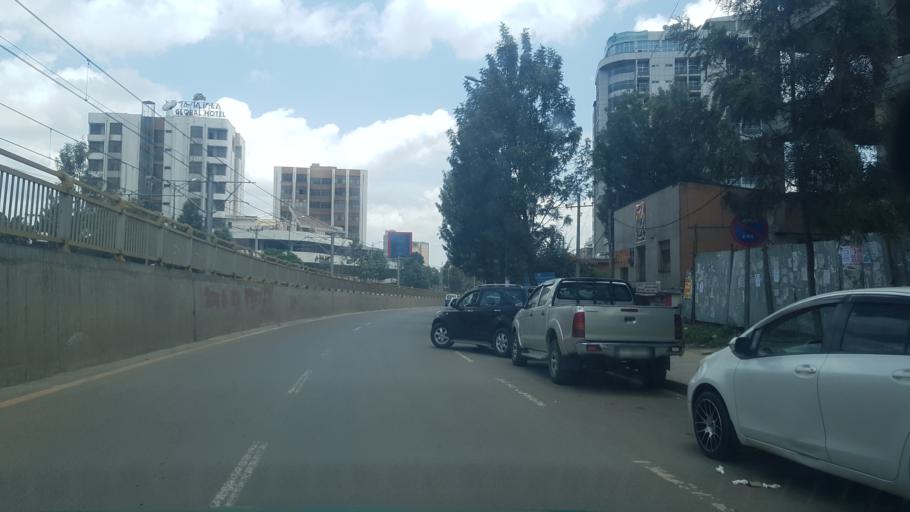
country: ET
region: Adis Abeba
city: Addis Ababa
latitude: 8.9949
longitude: 38.7597
